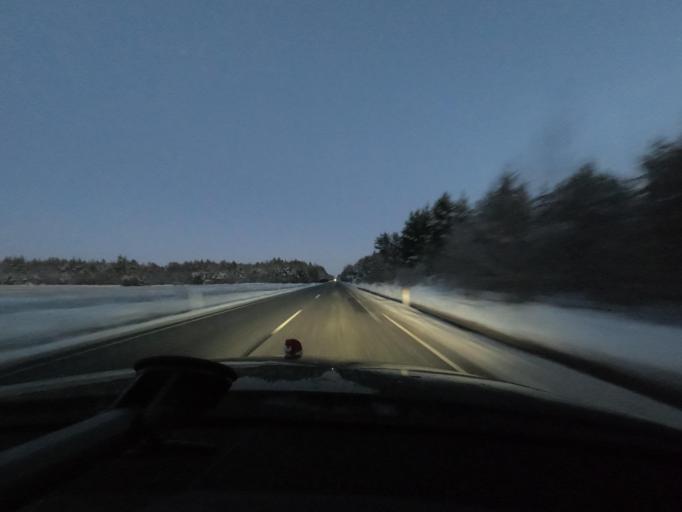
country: DK
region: South Denmark
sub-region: Tonder Kommune
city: Sherrebek
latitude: 55.1760
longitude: 8.8343
